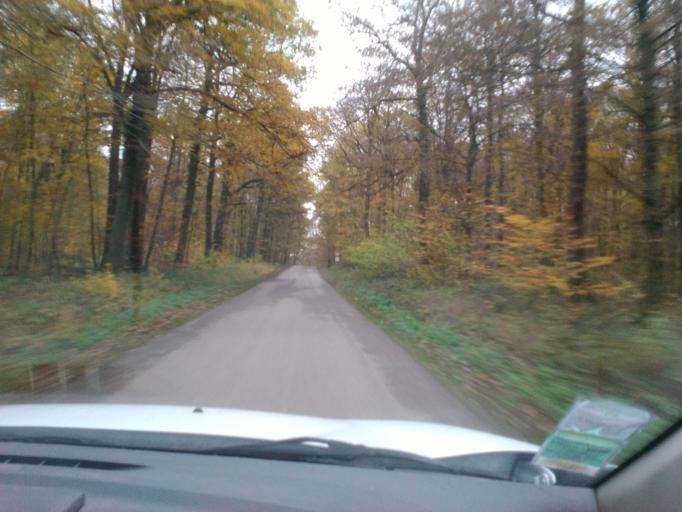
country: FR
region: Lorraine
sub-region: Departement des Vosges
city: Mirecourt
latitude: 48.2987
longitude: 6.2115
